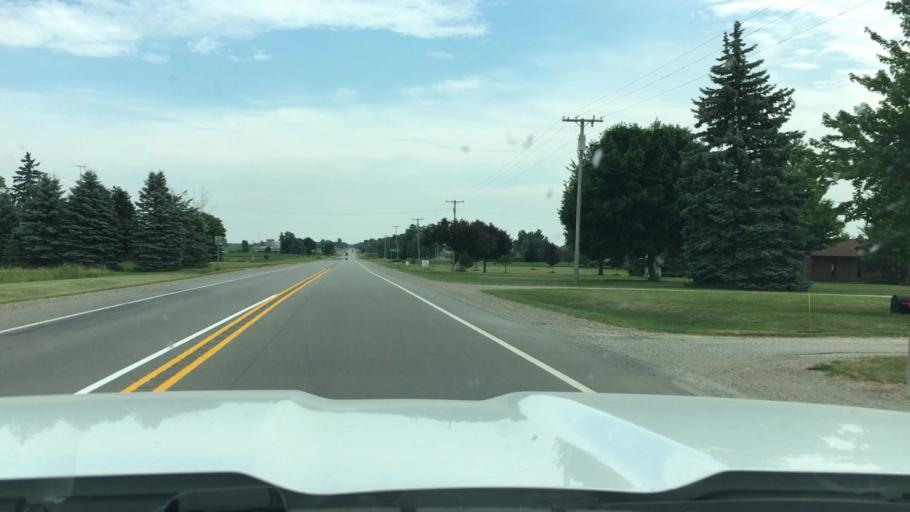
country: US
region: Michigan
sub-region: Sanilac County
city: Marlette
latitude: 43.3747
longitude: -83.0857
